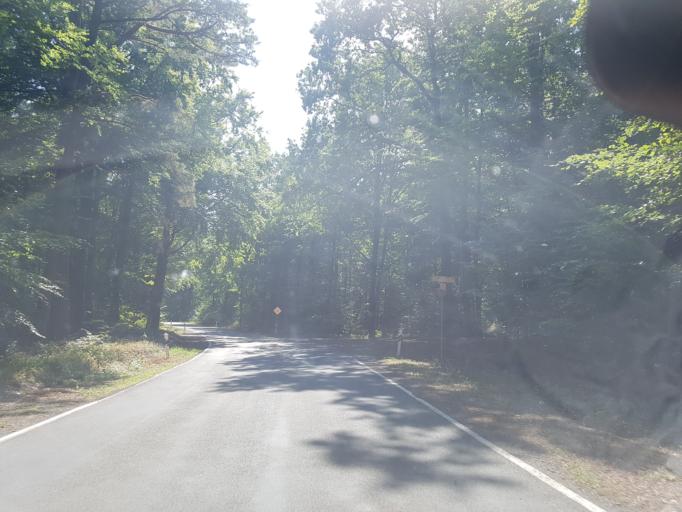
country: DE
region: Brandenburg
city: Wiesenburg
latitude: 52.0414
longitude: 12.3766
